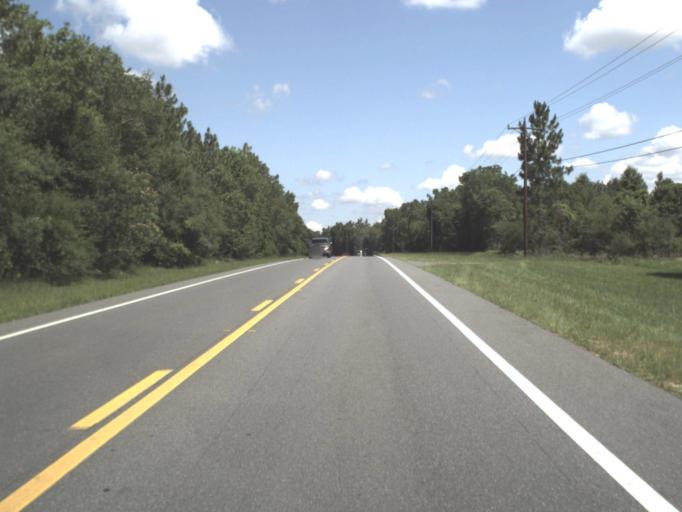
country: US
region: Florida
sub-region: Clay County
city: Keystone Heights
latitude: 29.7547
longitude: -81.9968
